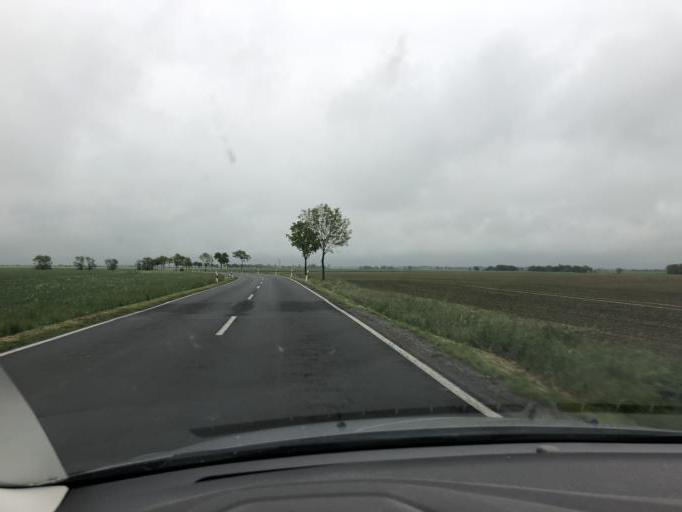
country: DE
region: Saxony
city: Zschortau
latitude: 51.4993
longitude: 12.3897
